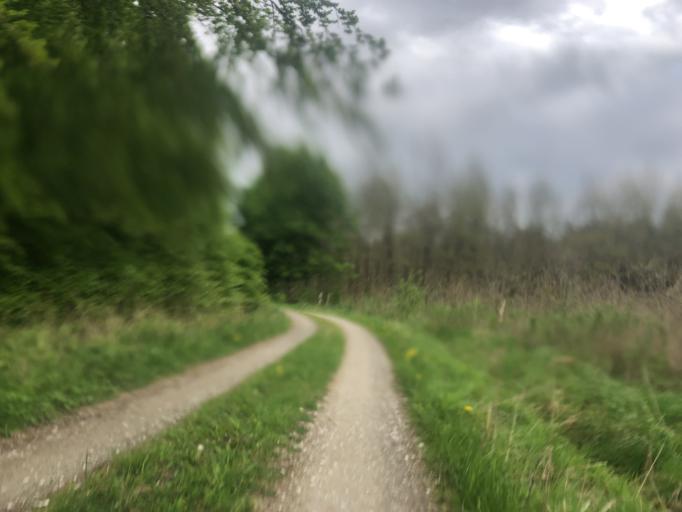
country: DK
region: Zealand
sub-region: Koge Kommune
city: Ejby
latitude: 55.4419
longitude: 12.0919
